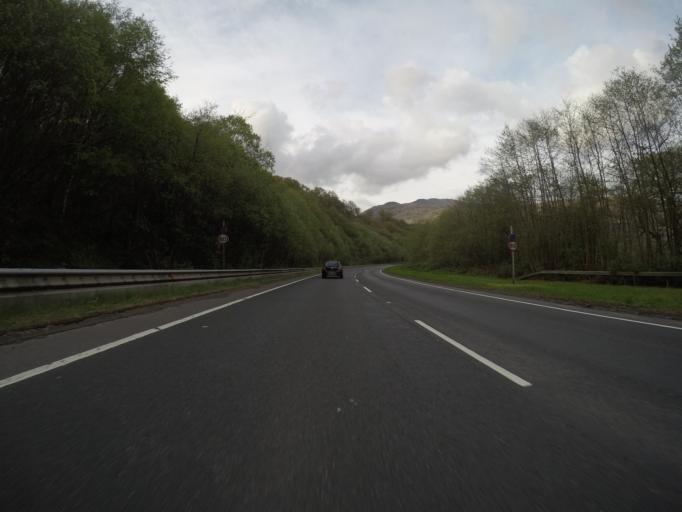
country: GB
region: Scotland
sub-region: Argyll and Bute
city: Helensburgh
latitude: 56.1590
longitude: -4.6712
